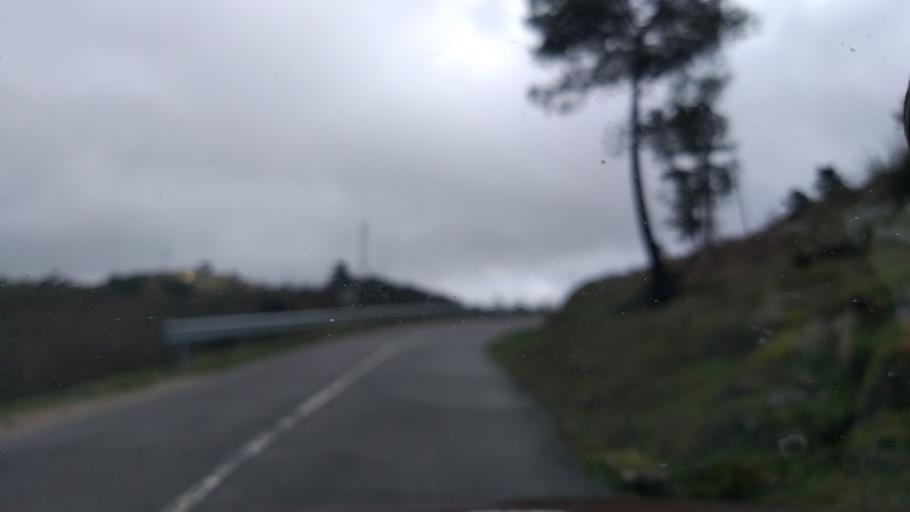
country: PT
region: Guarda
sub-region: Celorico da Beira
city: Celorico da Beira
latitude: 40.7124
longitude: -7.4202
